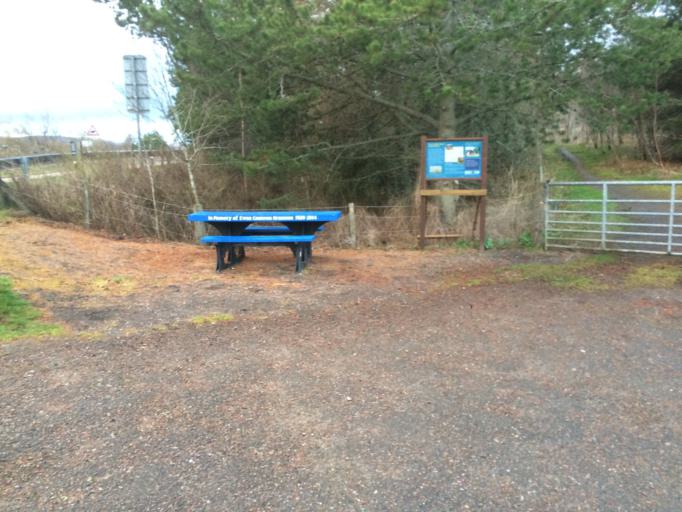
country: GB
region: Scotland
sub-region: Highland
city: Kingussie
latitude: 57.0613
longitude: -4.1355
